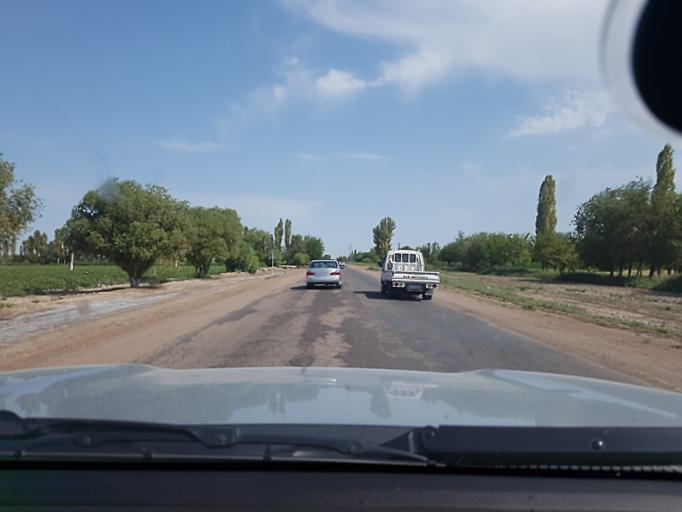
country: TM
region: Dasoguz
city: Boldumsaz
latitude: 42.1172
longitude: 59.6840
